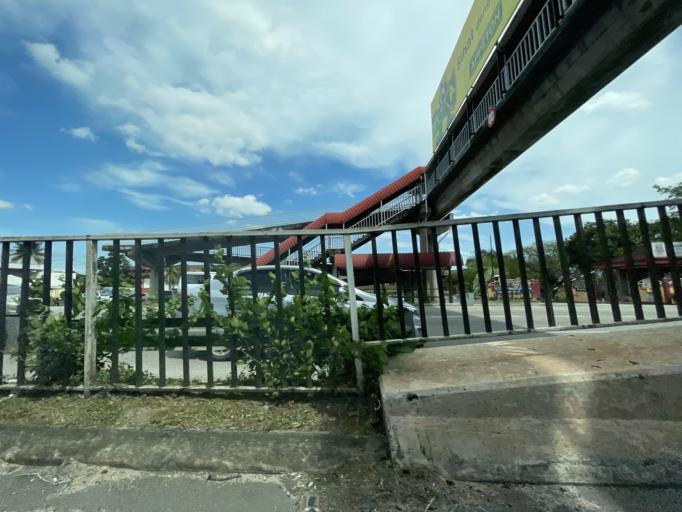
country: MY
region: Melaka
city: Batu Berendam
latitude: 2.2507
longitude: 102.2229
